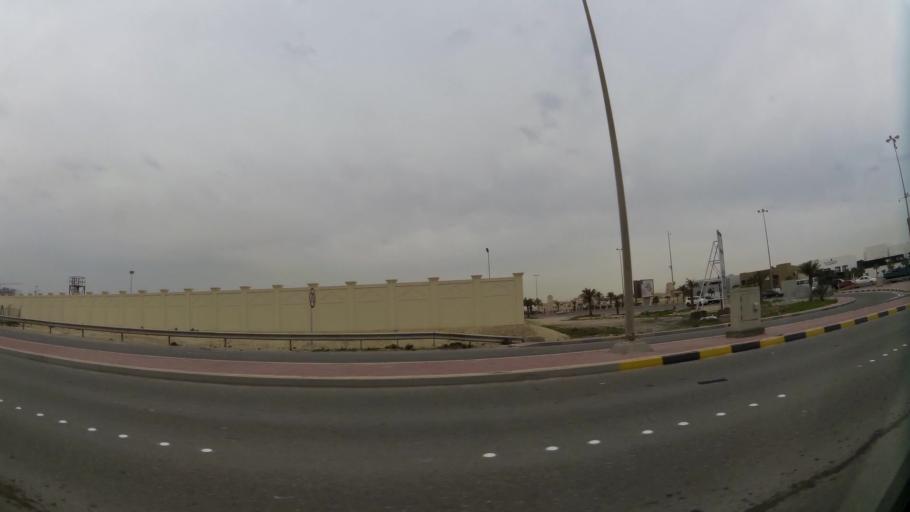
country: BH
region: Northern
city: Ar Rifa'
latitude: 26.1007
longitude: 50.5542
